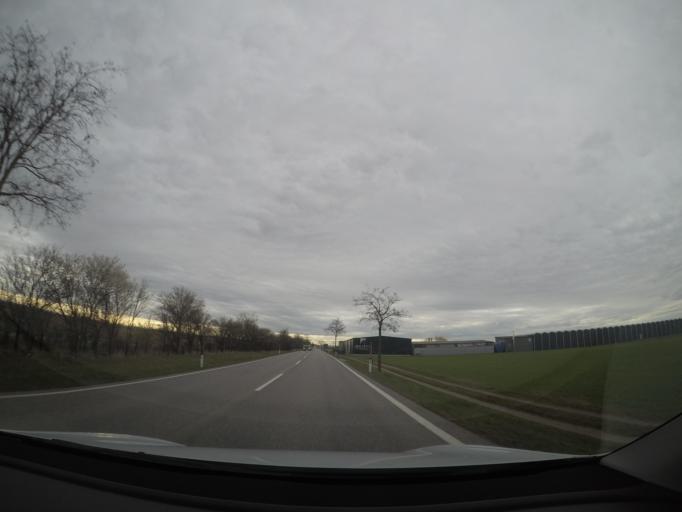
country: AT
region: Lower Austria
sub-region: Politischer Bezirk Modling
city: Munchendorf
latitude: 48.0492
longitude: 16.3819
